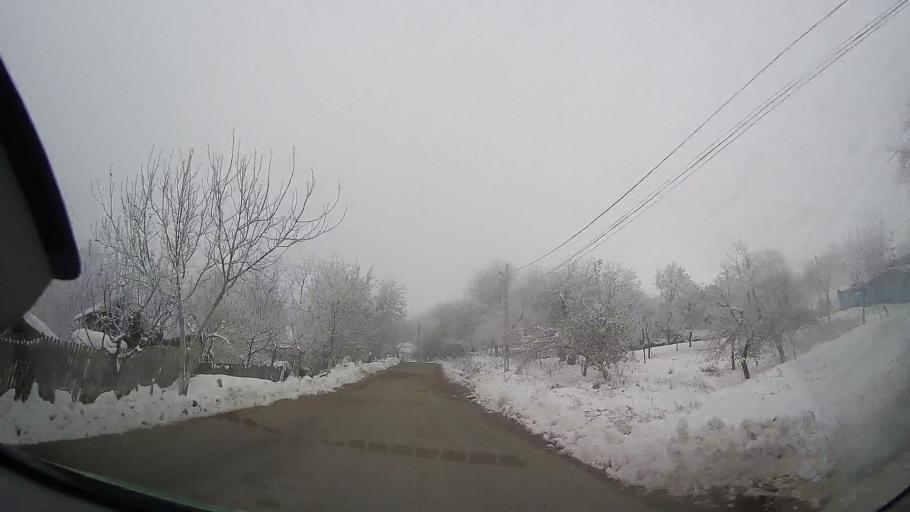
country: RO
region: Iasi
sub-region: Comuna Tansa
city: Suhulet
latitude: 46.8938
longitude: 27.2831
